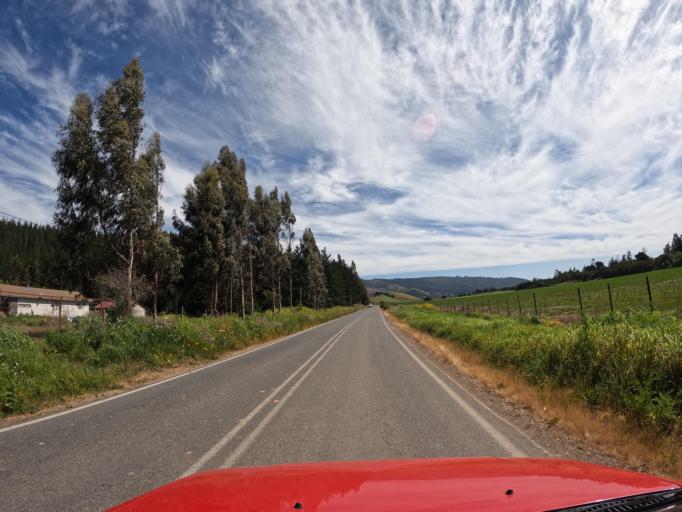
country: CL
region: Maule
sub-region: Provincia de Talca
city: Constitucion
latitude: -35.0346
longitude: -72.0540
